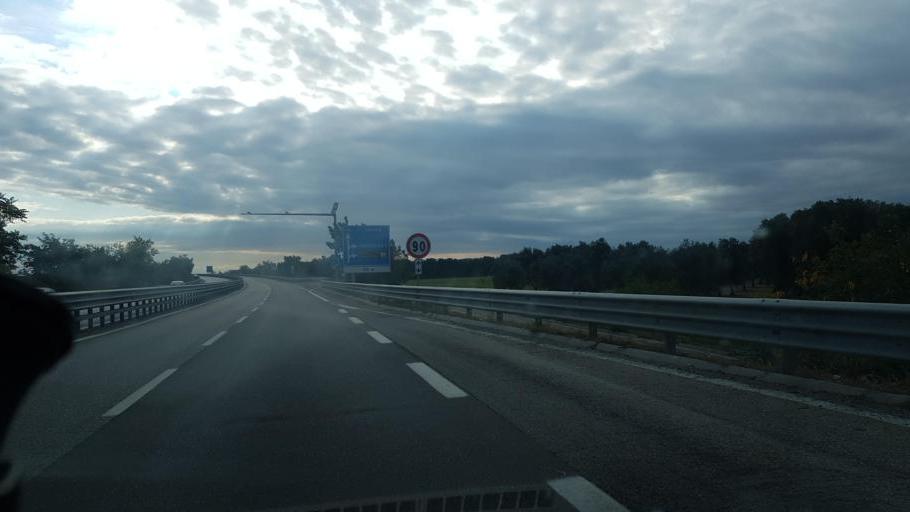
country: IT
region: Apulia
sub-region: Provincia di Brindisi
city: Francavilla Fontana
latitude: 40.5432
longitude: 17.5376
